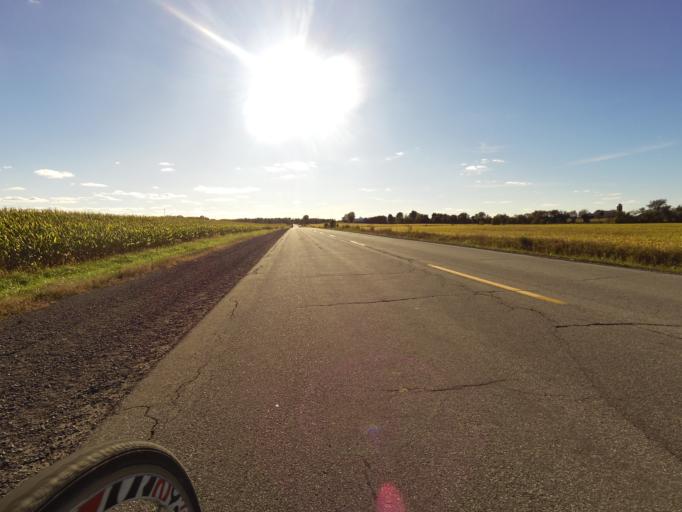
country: CA
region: Ontario
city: Bells Corners
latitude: 45.1835
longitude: -75.8013
